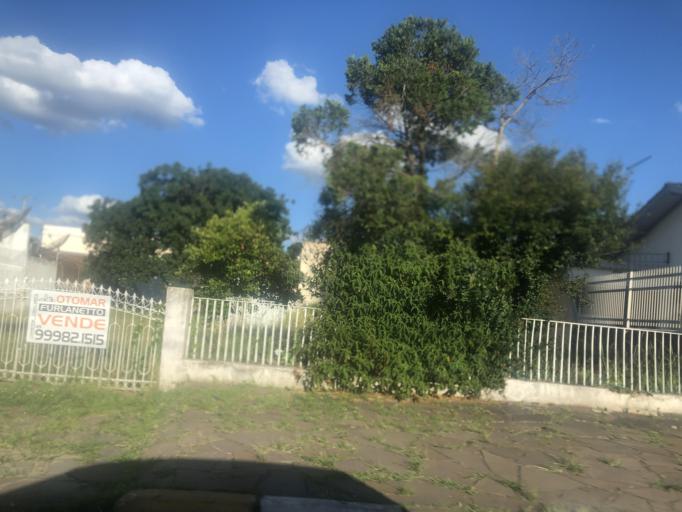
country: BR
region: Santa Catarina
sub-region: Lages
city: Lages
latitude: -27.8156
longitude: -50.3137
